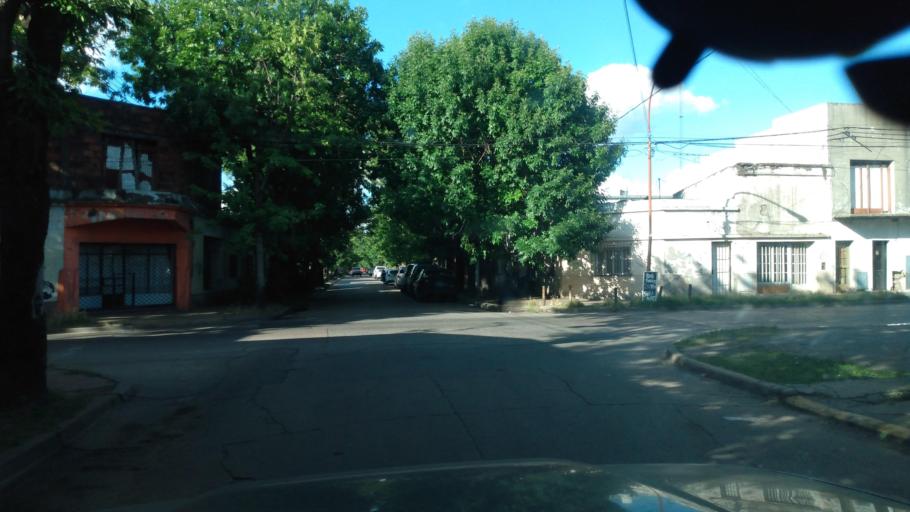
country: AR
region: Buenos Aires
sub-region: Partido de Lujan
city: Lujan
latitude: -34.5691
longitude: -59.1086
